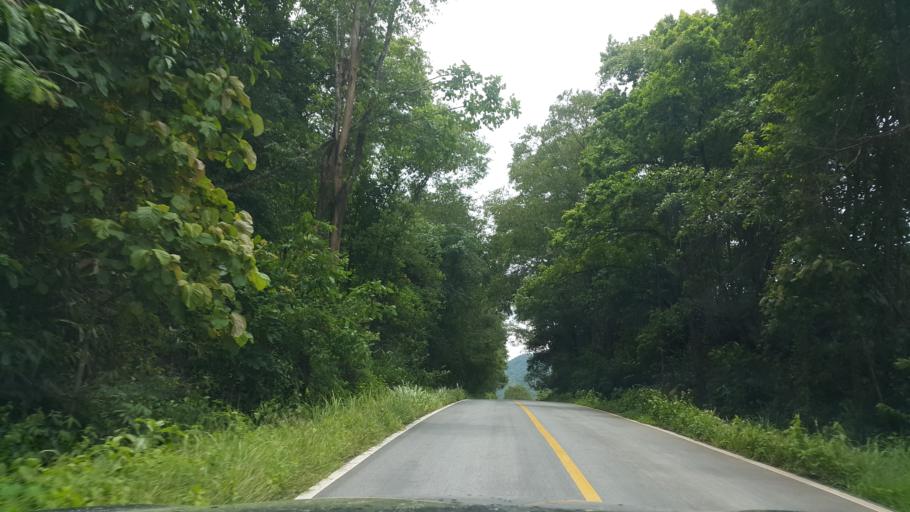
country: TH
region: Phitsanulok
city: Chat Trakan
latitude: 17.3519
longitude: 100.7253
